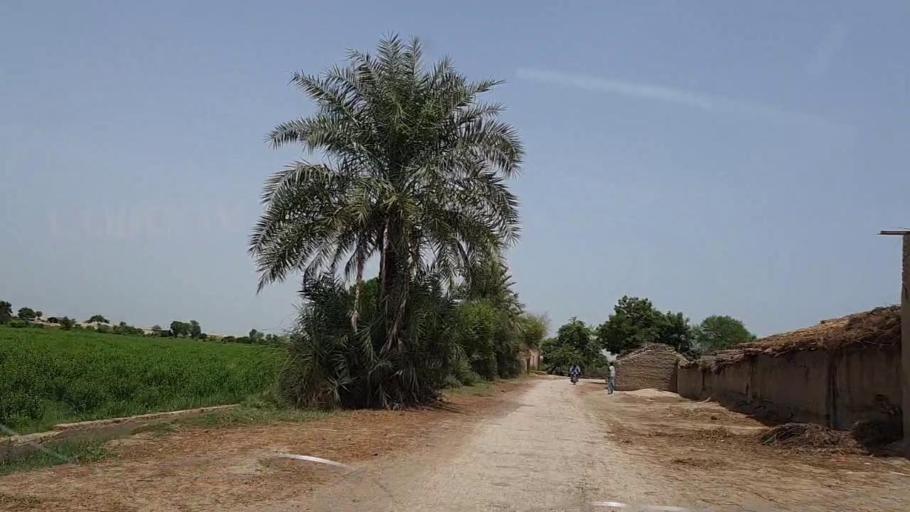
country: PK
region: Sindh
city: Tharu Shah
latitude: 26.9674
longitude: 68.0348
